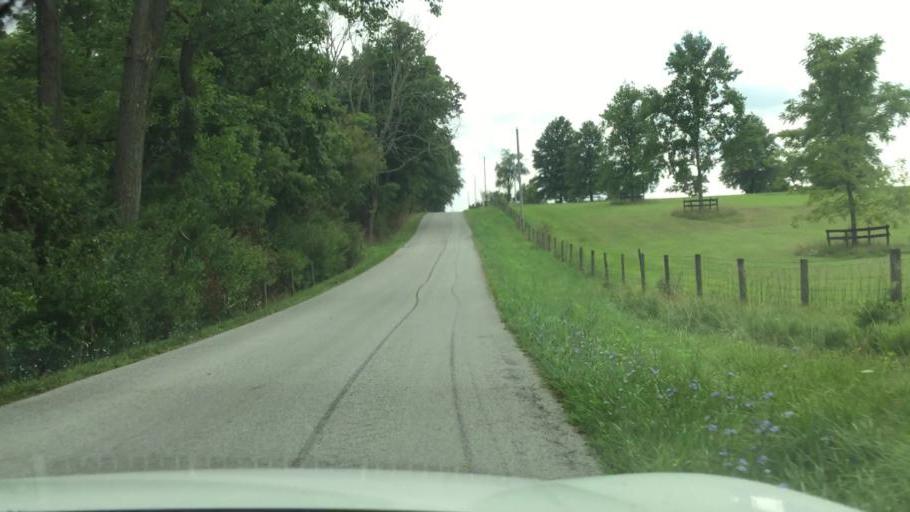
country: US
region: Ohio
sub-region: Champaign County
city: Mechanicsburg
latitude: 40.0036
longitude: -83.6555
